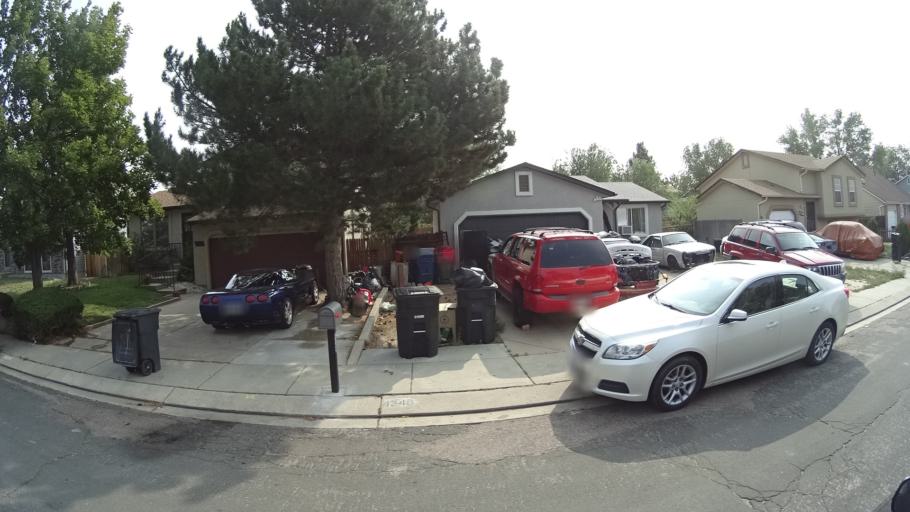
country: US
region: Colorado
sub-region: El Paso County
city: Stratmoor
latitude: 38.8058
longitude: -104.7471
